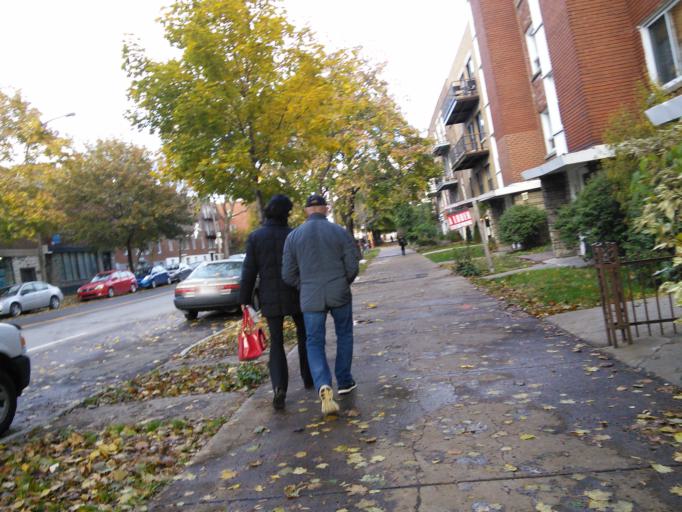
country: CA
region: Quebec
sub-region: Montreal
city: Montreal
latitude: 45.5292
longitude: -73.5882
